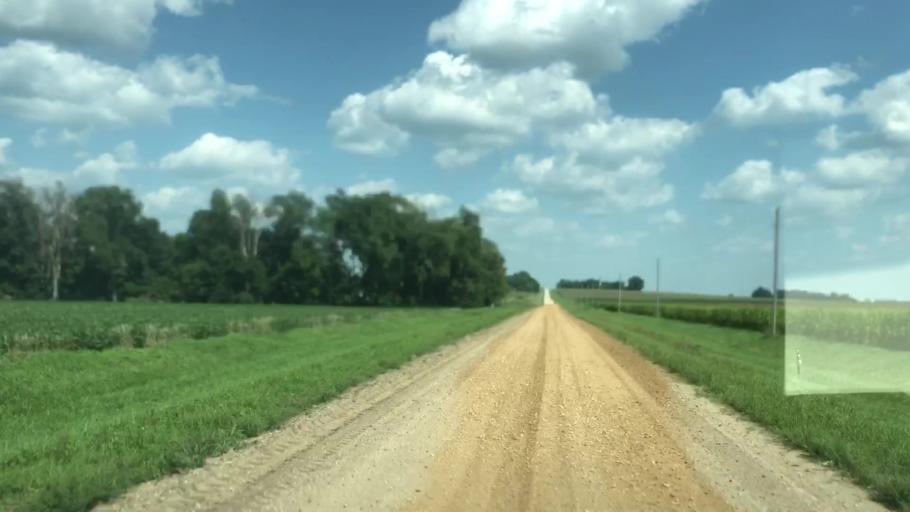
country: US
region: Iowa
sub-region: O'Brien County
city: Sheldon
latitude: 43.1569
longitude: -95.7885
